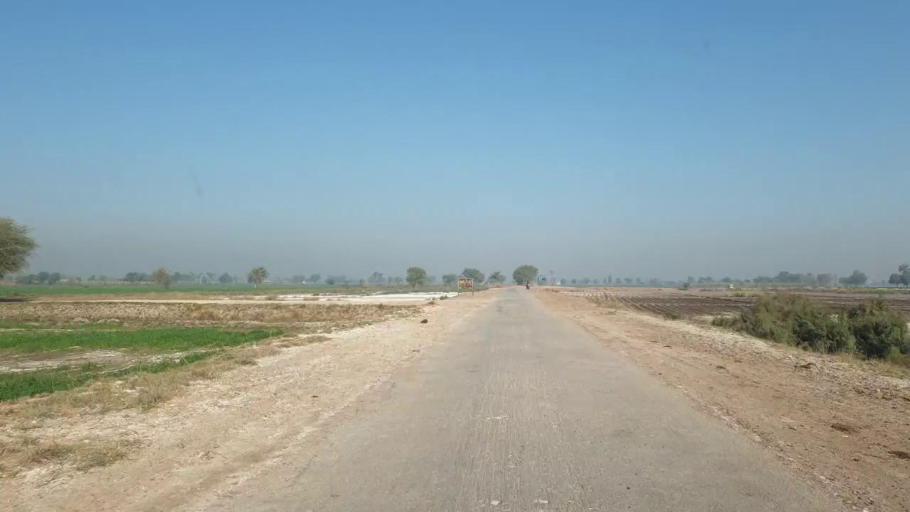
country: PK
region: Sindh
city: Shahdadpur
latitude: 25.9447
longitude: 68.5028
